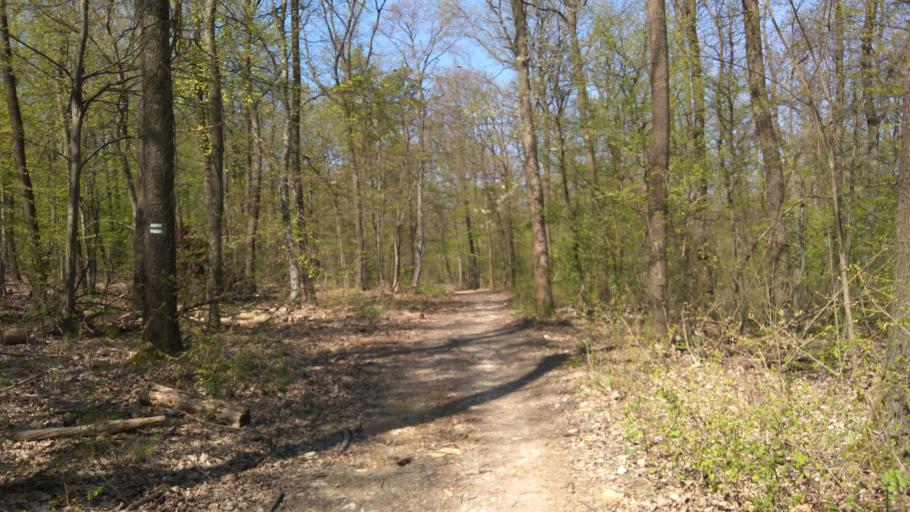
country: HU
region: Pest
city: Pilisborosjeno
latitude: 47.6271
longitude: 18.9869
